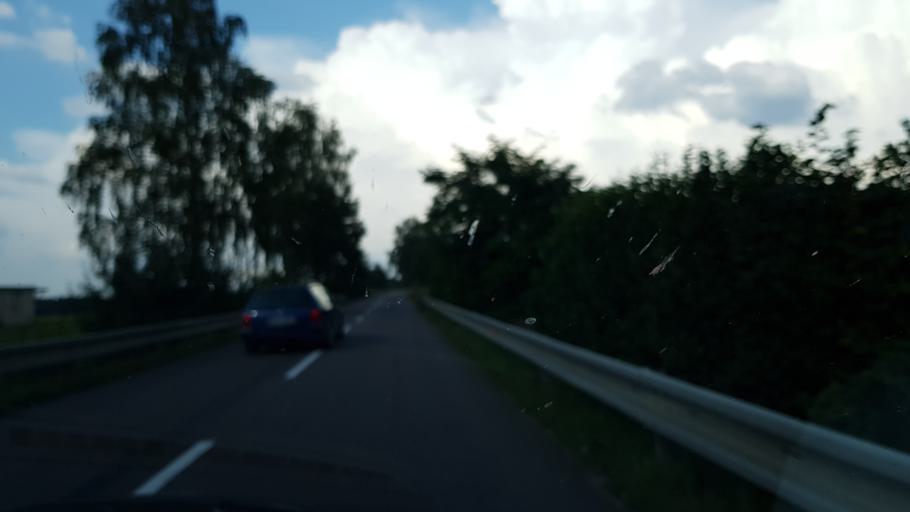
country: CZ
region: Pardubicky
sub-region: Okres Usti nad Orlici
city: Kunvald
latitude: 50.0867
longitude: 16.5244
